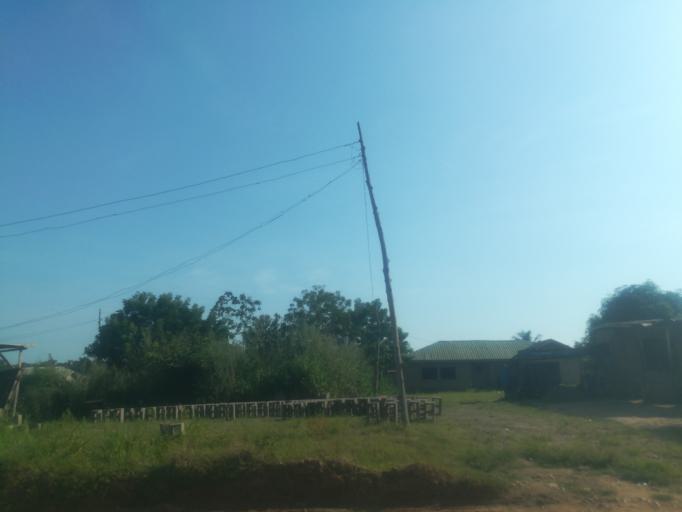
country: NG
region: Ogun
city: Abeokuta
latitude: 7.1403
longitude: 3.2558
